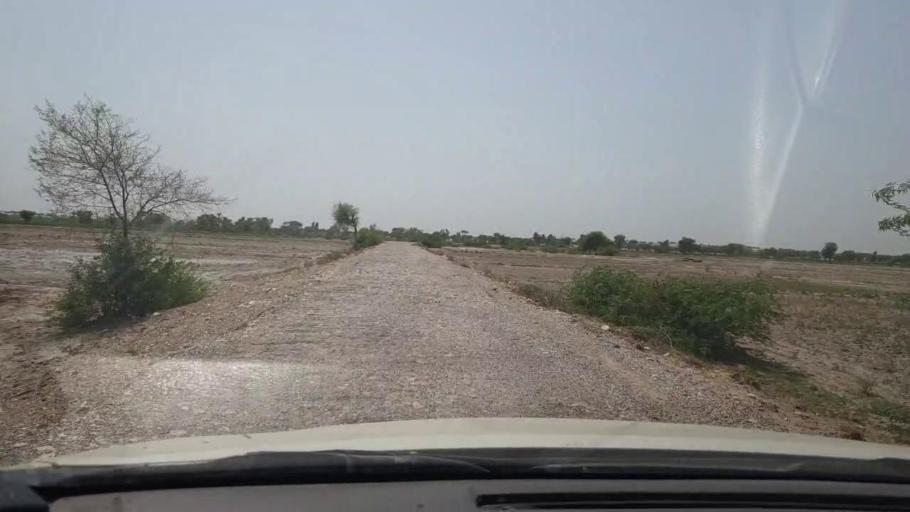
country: PK
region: Sindh
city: Rohri
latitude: 27.5212
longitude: 69.0980
